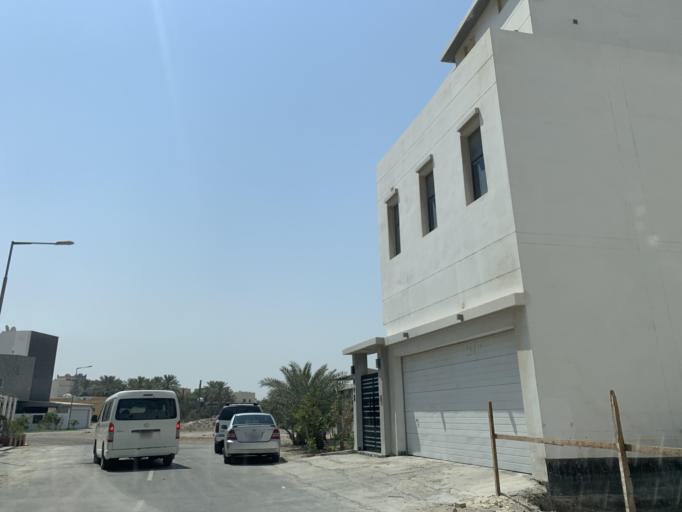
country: BH
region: Manama
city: Jidd Hafs
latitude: 26.2044
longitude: 50.5181
